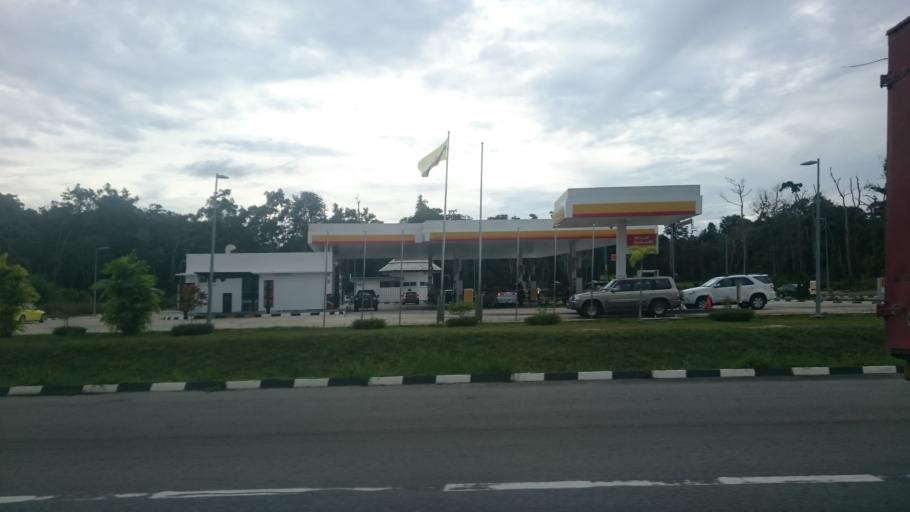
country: BN
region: Tutong
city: Tutong
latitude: 4.7785
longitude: 114.6538
